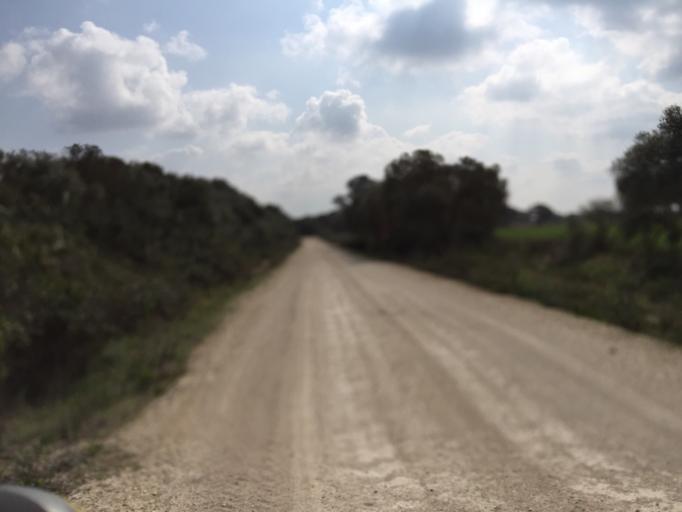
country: ES
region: Andalusia
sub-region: Provincia de Cadiz
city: Benalup-Casas Viejas
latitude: 36.3263
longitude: -5.8860
